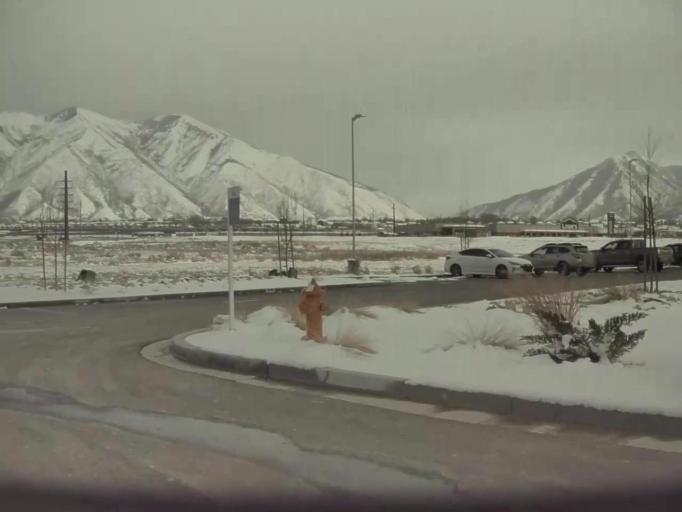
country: US
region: Utah
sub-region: Utah County
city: Spanish Fork
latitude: 40.1312
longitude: -111.6397
